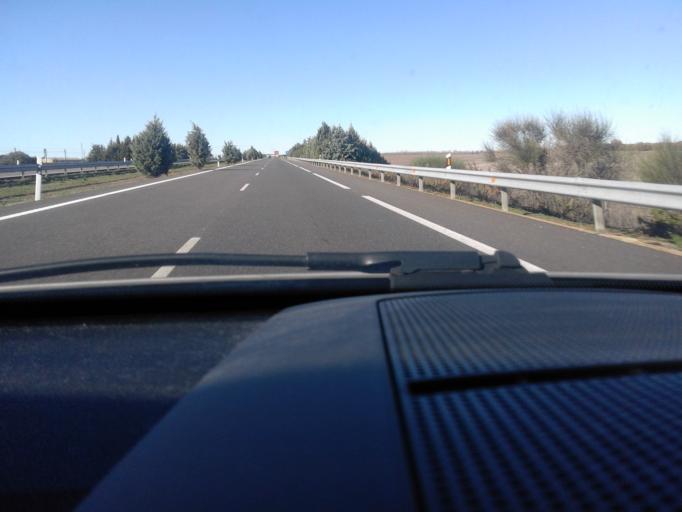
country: ES
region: Castille and Leon
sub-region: Provincia de Leon
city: Bercianos del Real Camino
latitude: 42.3902
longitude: -5.1220
